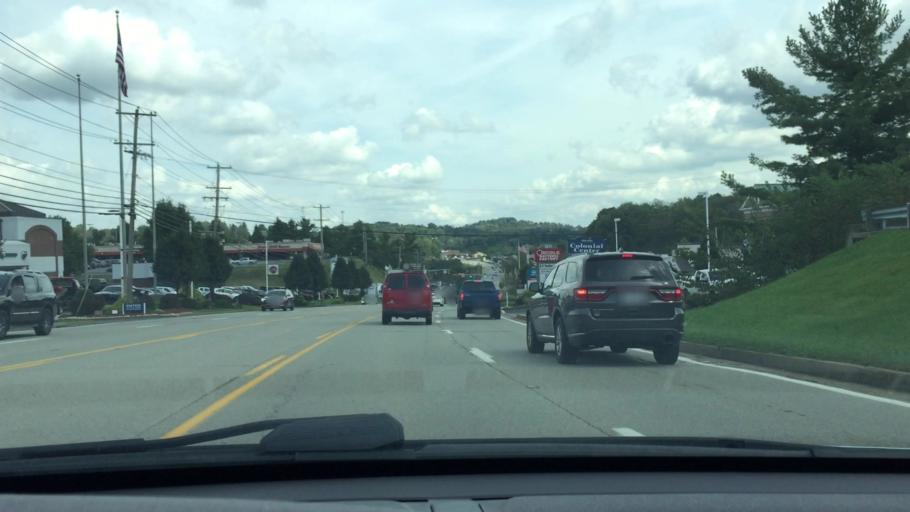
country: US
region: Pennsylvania
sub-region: Washington County
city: Thompsonville
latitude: 40.2885
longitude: -80.1148
